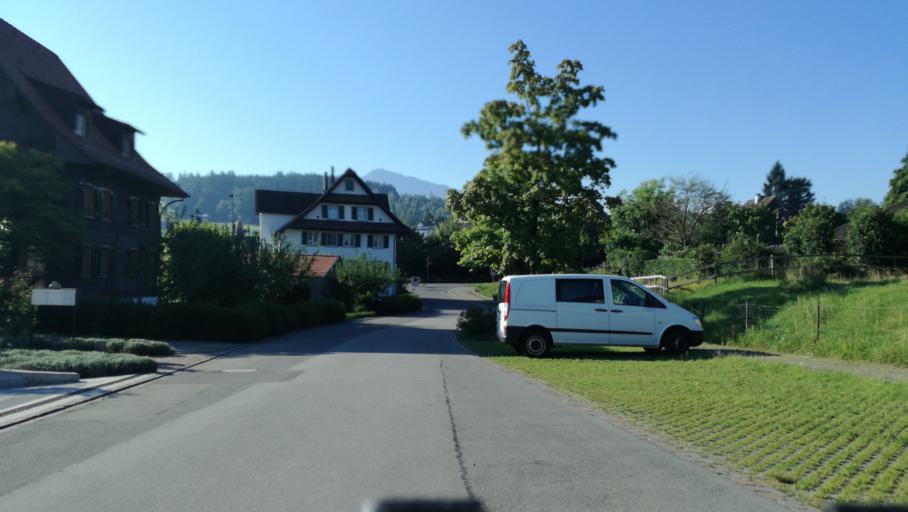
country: CH
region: Lucerne
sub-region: Lucerne-Land District
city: Meierskappel
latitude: 47.1430
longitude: 8.4557
